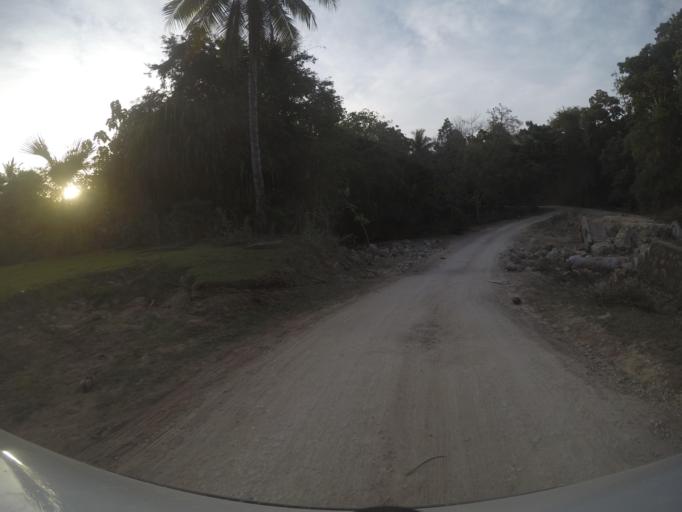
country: TL
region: Viqueque
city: Viqueque
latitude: -8.9438
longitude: 126.4527
